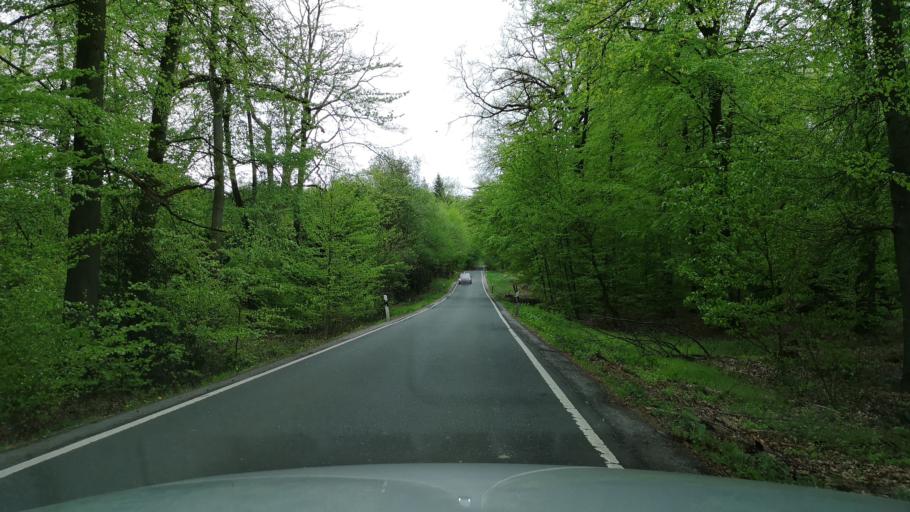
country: DE
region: North Rhine-Westphalia
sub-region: Regierungsbezirk Arnsberg
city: Frondenberg
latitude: 51.4564
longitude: 7.7073
